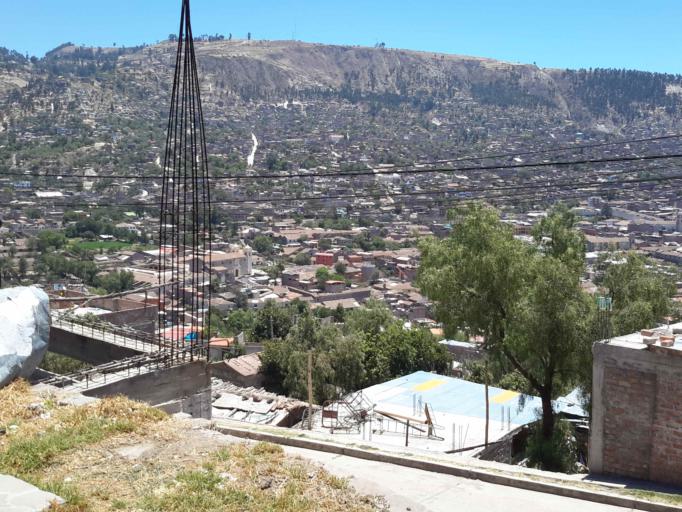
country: PE
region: Ayacucho
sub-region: Provincia de Huamanga
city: Ayacucho
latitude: -13.1702
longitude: -74.2231
